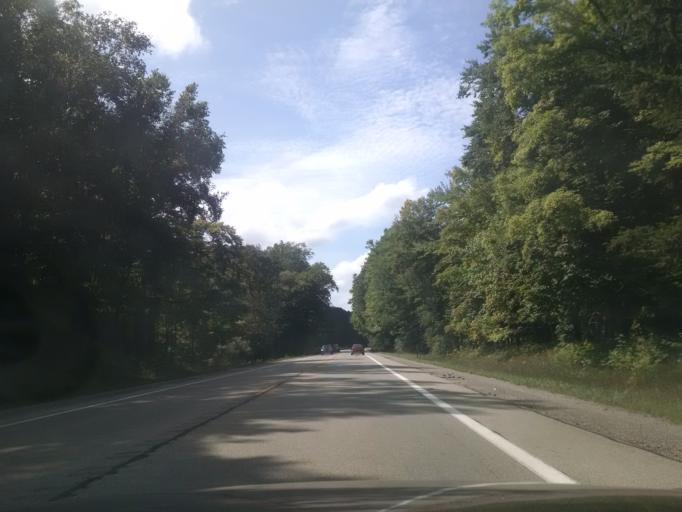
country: US
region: Michigan
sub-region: Clare County
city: Clare
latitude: 43.8706
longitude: -84.9305
